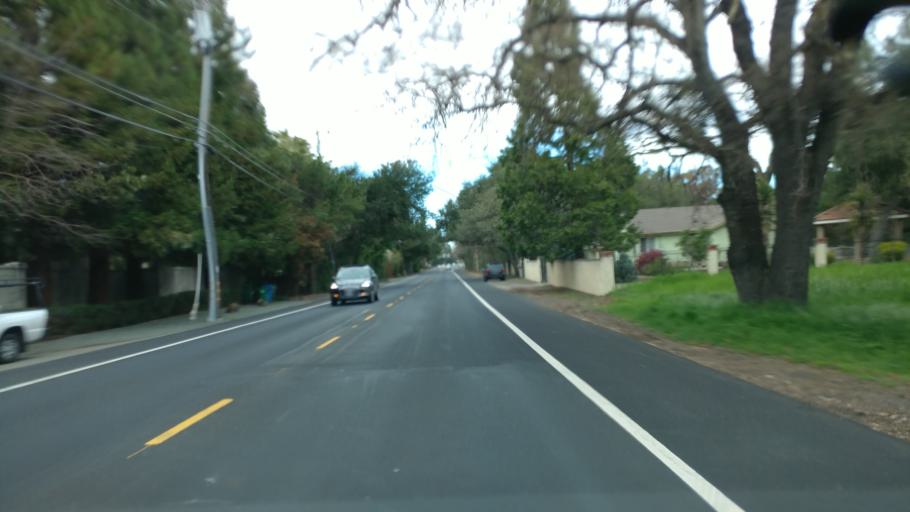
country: US
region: California
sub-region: Contra Costa County
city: Alamo
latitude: 37.8751
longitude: -122.0479
